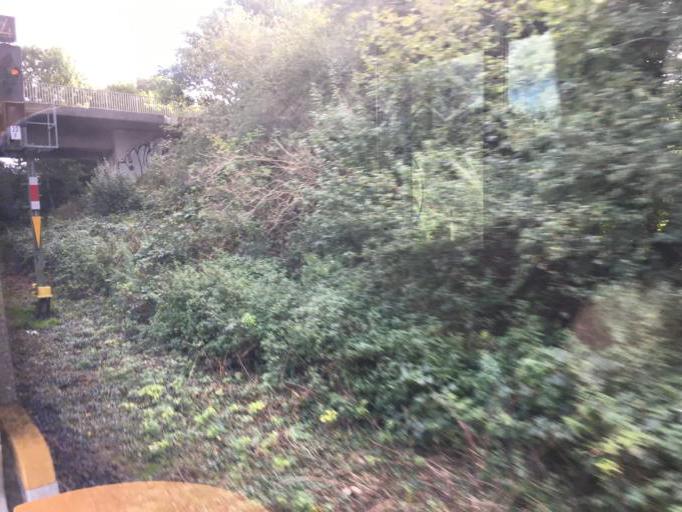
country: DE
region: Schleswig-Holstein
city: Kronshagen
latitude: 54.3146
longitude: 10.0900
